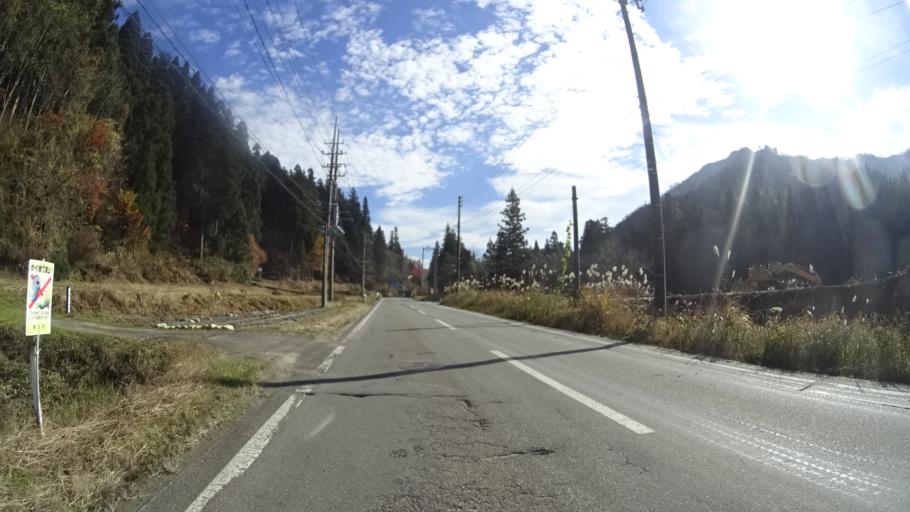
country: JP
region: Niigata
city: Muikamachi
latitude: 37.2235
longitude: 139.0243
